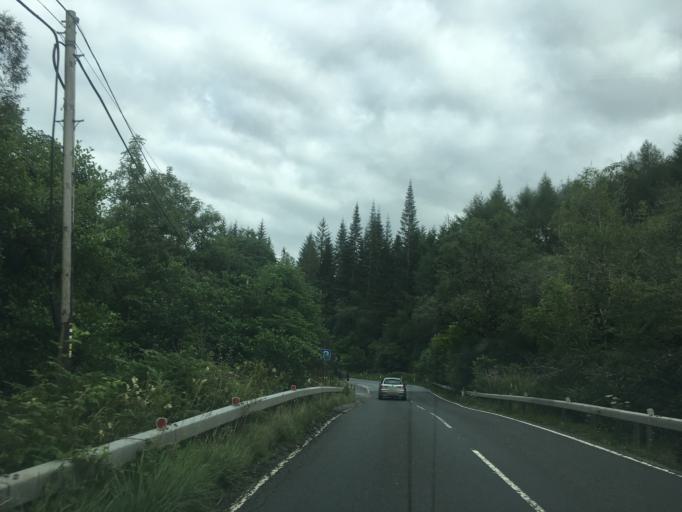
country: GB
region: Scotland
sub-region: Argyll and Bute
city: Oban
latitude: 56.3128
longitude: -5.4795
